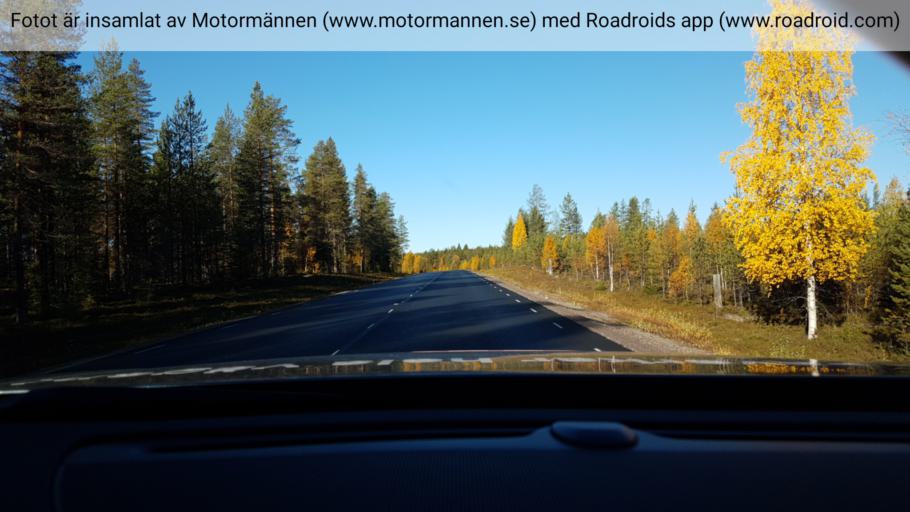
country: SE
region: Vaesterbotten
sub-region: Skelleftea Kommun
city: Langsele
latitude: 65.3894
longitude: 20.0440
